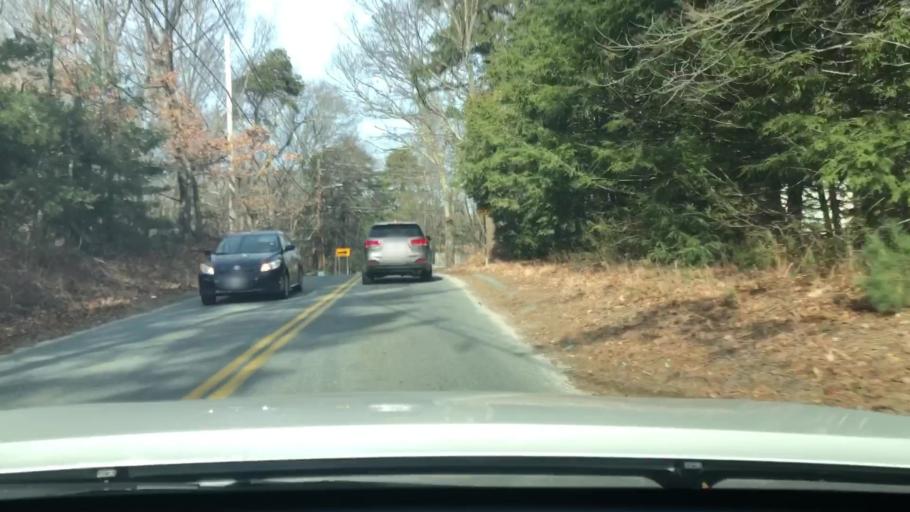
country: US
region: Massachusetts
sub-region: Worcester County
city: Milford
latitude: 42.1354
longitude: -71.4904
